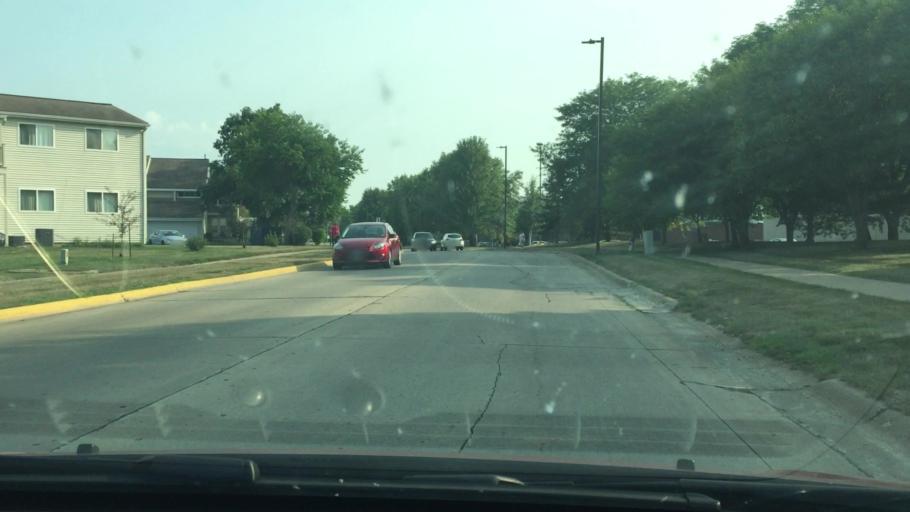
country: US
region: Iowa
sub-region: Muscatine County
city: Muscatine
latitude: 41.4509
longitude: -91.0352
